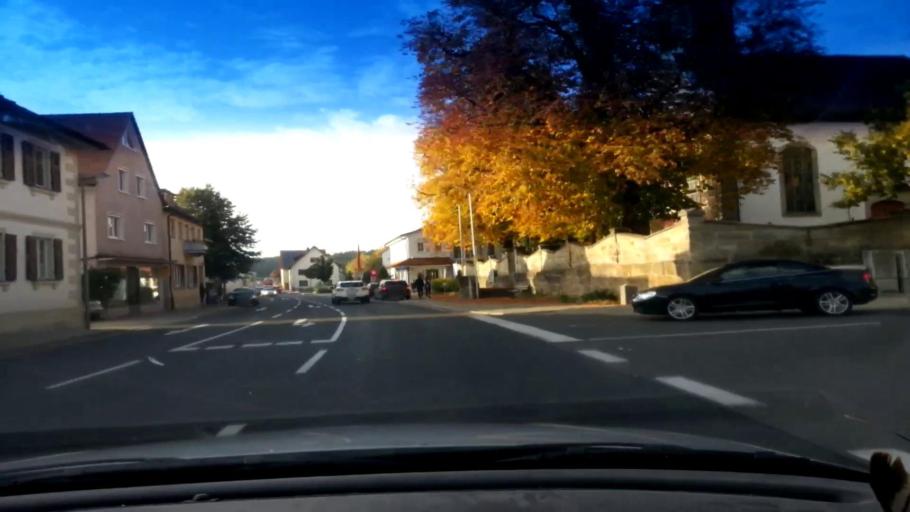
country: DE
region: Bavaria
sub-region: Upper Franconia
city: Strullendorf
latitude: 49.8450
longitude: 10.9685
